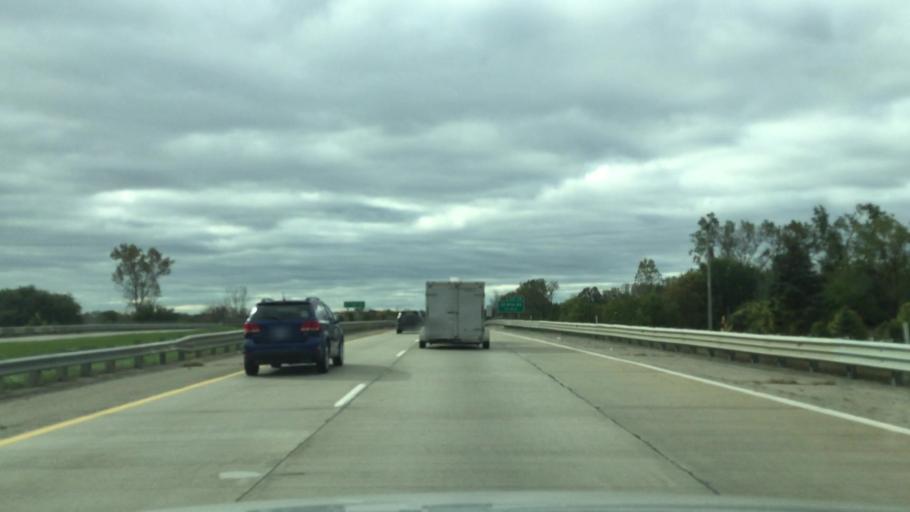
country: US
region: Michigan
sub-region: Macomb County
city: Shelby
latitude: 42.7293
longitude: -83.0269
